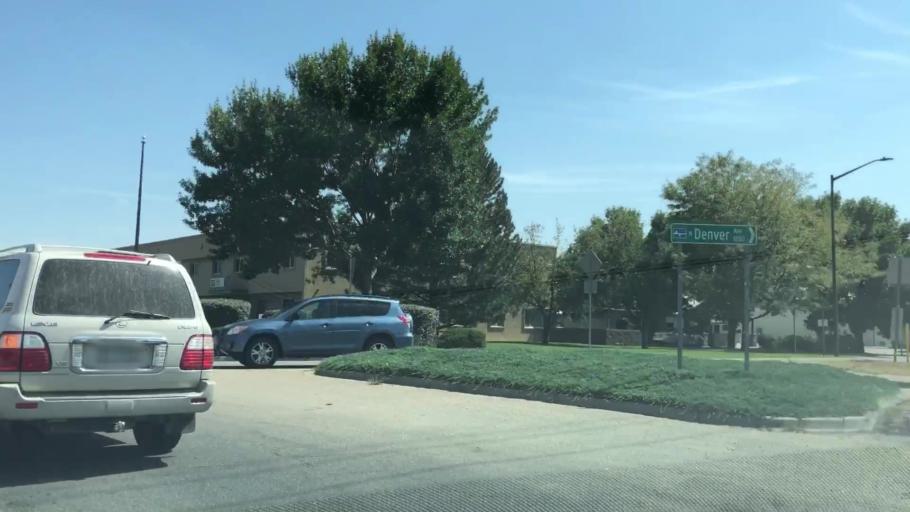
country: US
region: Colorado
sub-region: Larimer County
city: Loveland
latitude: 40.4051
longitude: -105.0448
